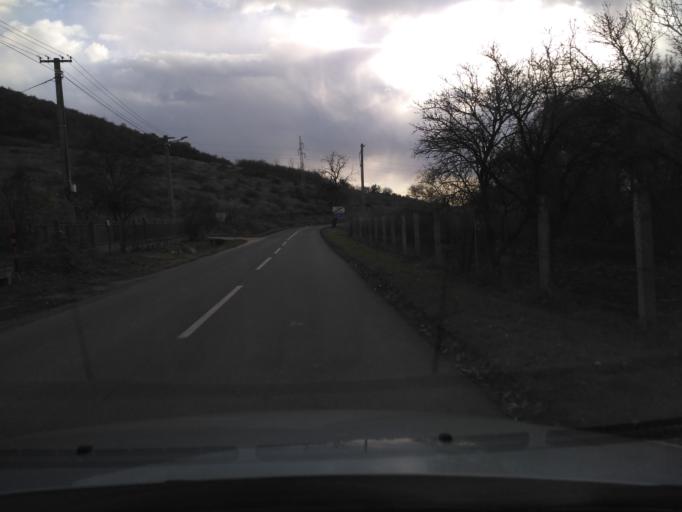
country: HU
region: Borsod-Abauj-Zemplen
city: Satoraljaujhely
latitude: 48.4201
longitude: 21.7267
